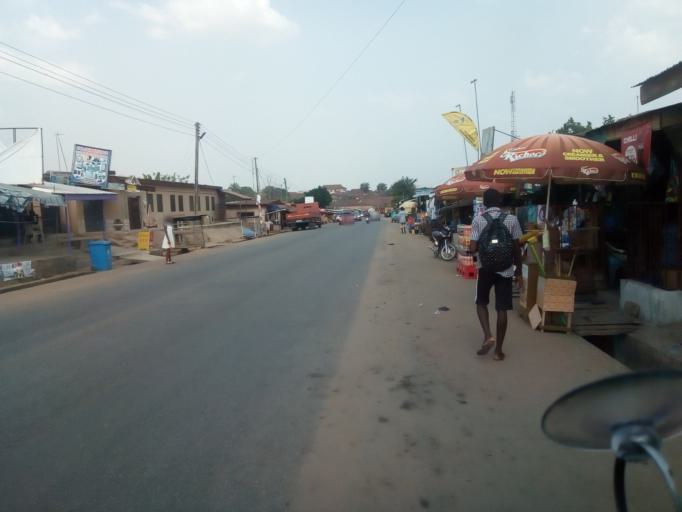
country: GH
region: Eastern
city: Suhum
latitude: 6.0365
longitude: -0.4547
